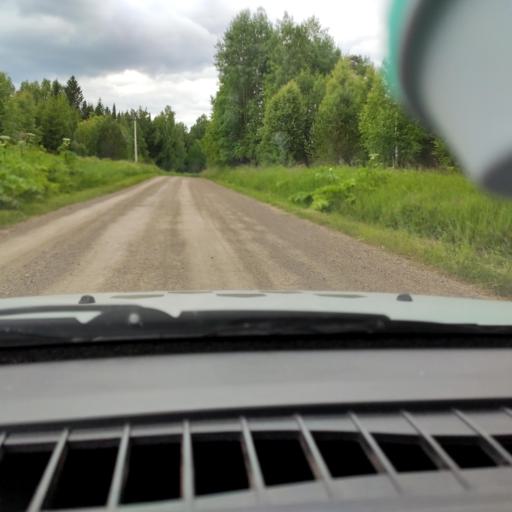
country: RU
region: Perm
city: Suksun
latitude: 57.2069
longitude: 57.6324
